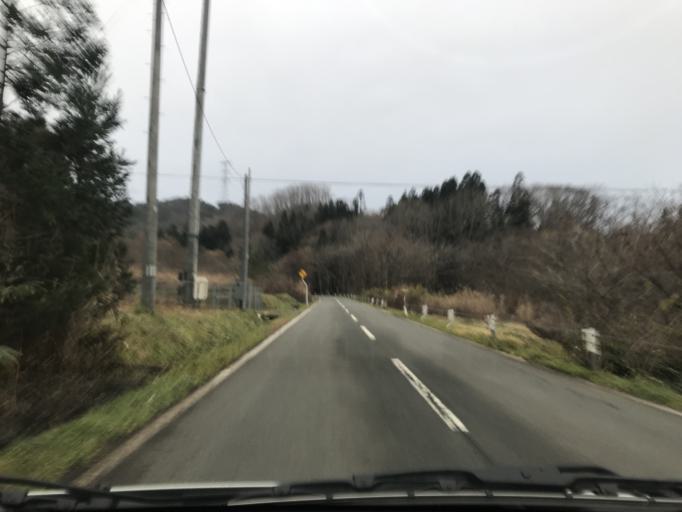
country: JP
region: Iwate
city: Tono
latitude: 39.1601
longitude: 141.3649
